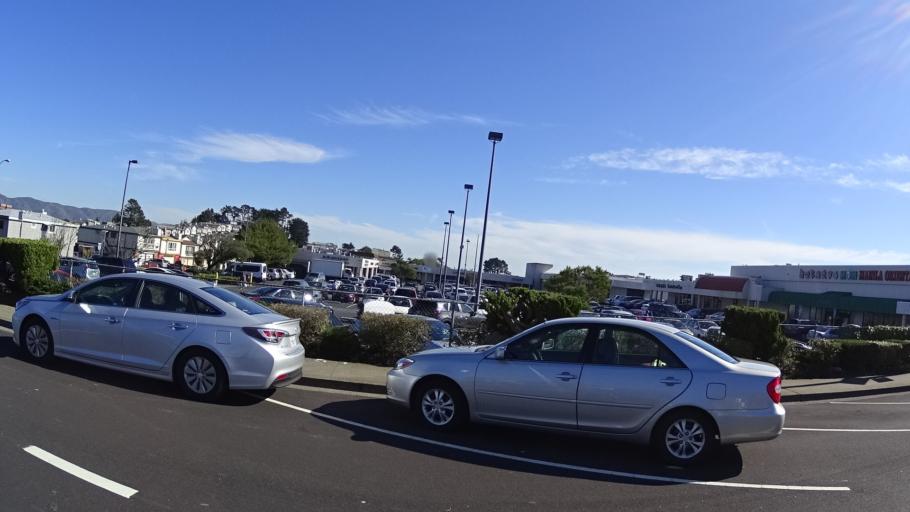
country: US
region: California
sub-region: San Mateo County
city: Colma
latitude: 37.6519
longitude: -122.4693
